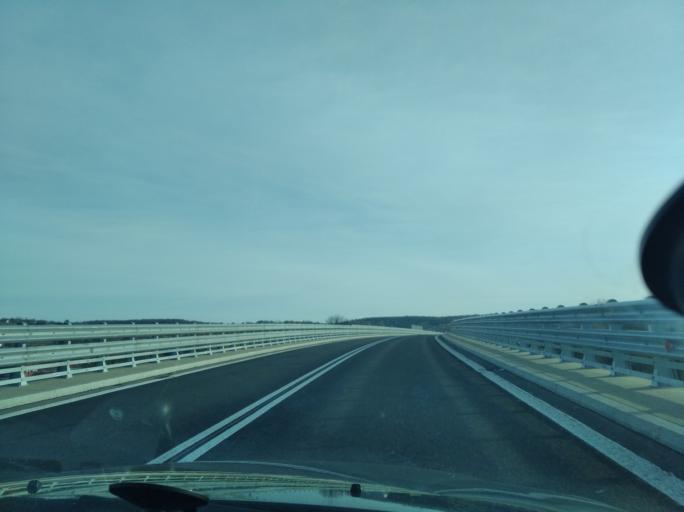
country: PL
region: Subcarpathian Voivodeship
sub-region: Powiat strzyzowski
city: Czudec
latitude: 49.9397
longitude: 21.8220
